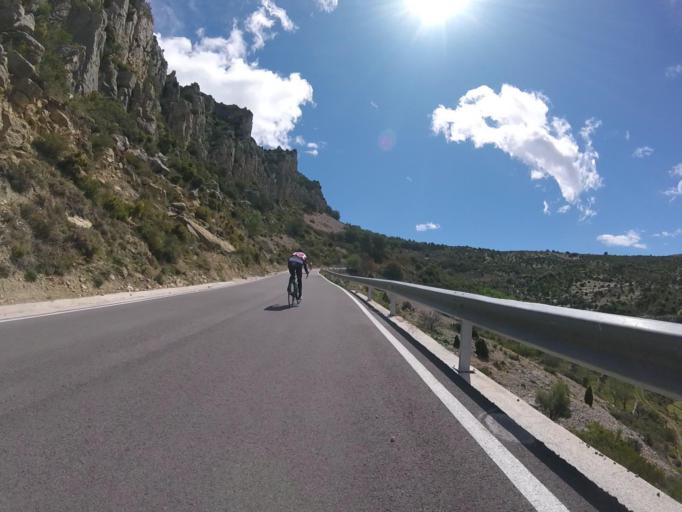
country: ES
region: Valencia
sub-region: Provincia de Castello
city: Sierra-Engarceran
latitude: 40.2840
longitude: -0.0342
